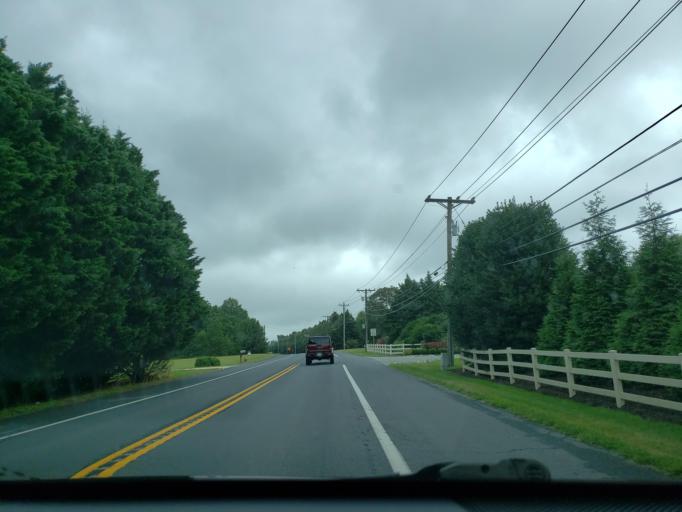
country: US
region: Delaware
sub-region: Sussex County
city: Lewes
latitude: 38.7601
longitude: -75.2236
